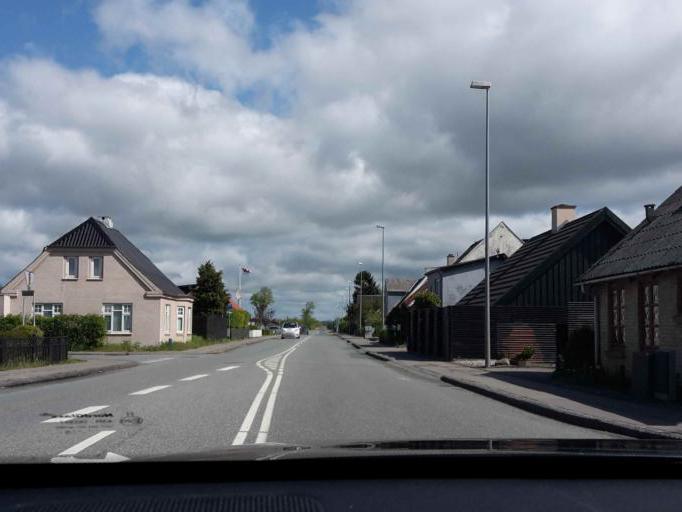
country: DK
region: Central Jutland
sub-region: Syddjurs Kommune
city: Hornslet
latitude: 56.3192
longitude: 10.3230
